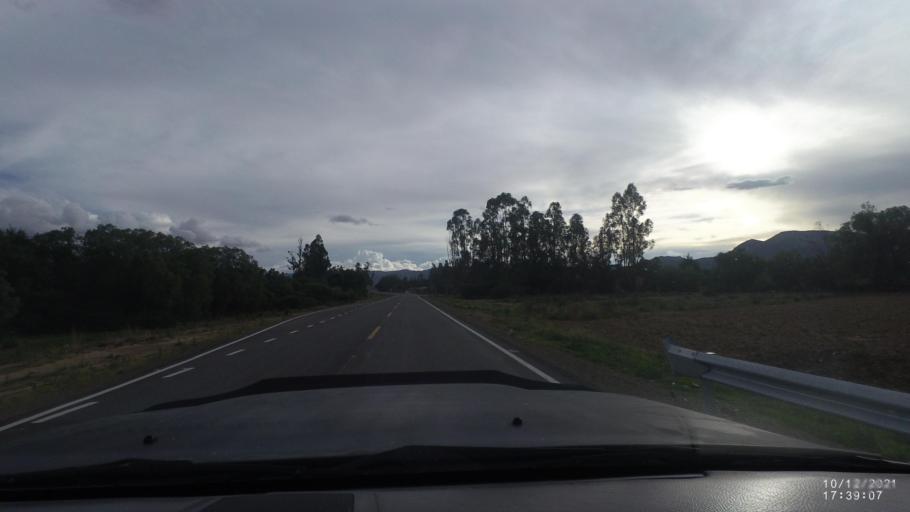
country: BO
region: Cochabamba
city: Tarata
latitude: -17.5760
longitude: -66.0129
